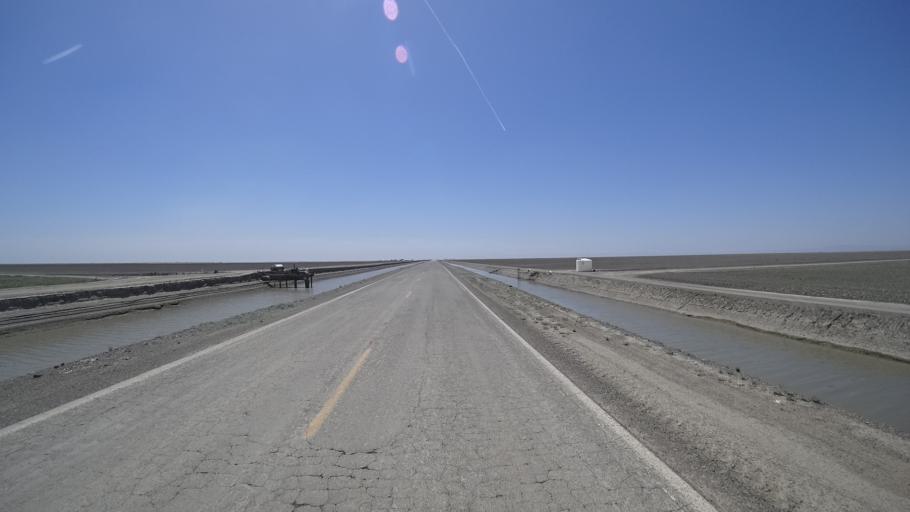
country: US
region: California
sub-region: Kings County
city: Corcoran
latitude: 36.0007
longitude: -119.6431
